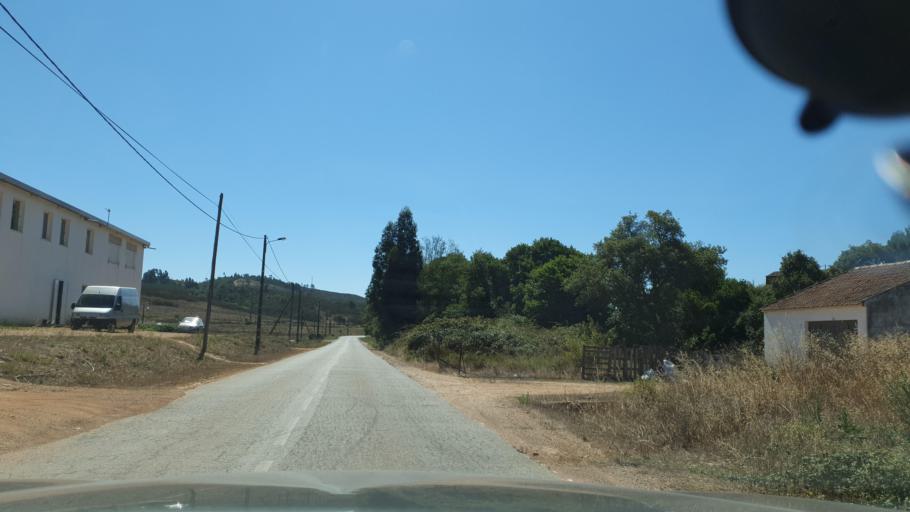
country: PT
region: Beja
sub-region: Odemira
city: Sao Teotonio
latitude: 37.4873
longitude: -8.6377
